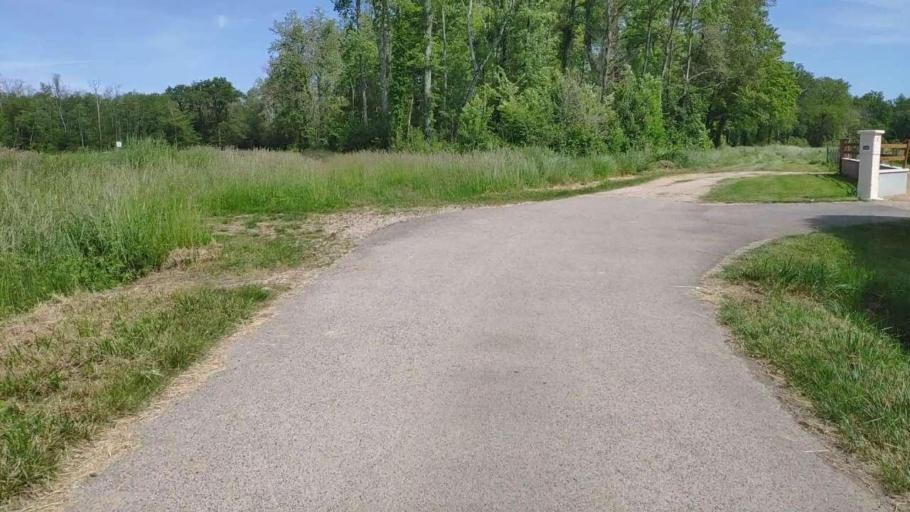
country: FR
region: Franche-Comte
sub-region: Departement du Jura
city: Bletterans
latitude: 46.7092
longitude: 5.4199
